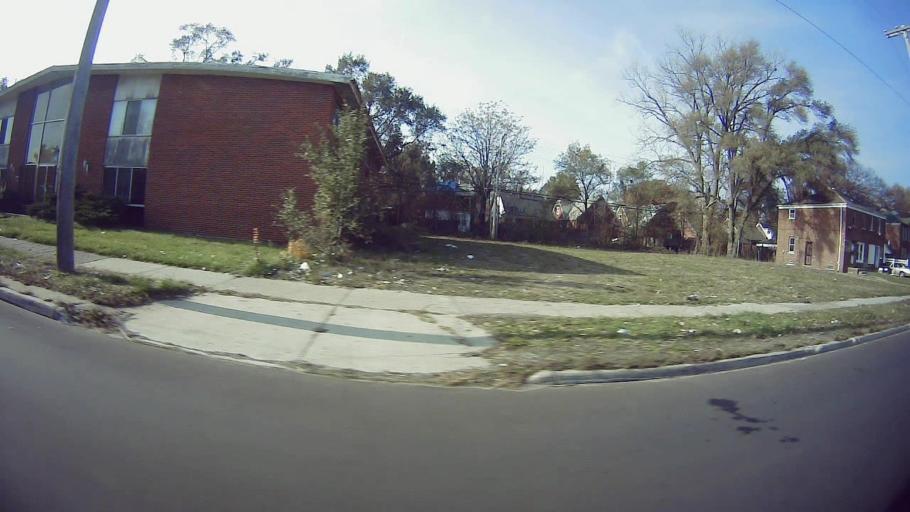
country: US
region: Michigan
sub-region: Oakland County
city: Oak Park
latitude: 42.4109
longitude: -83.1796
